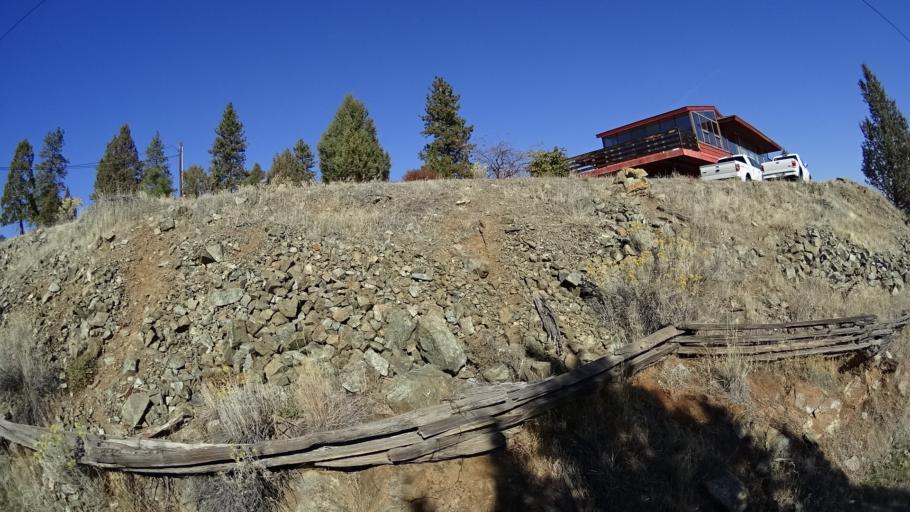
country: US
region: California
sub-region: Siskiyou County
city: Yreka
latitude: 41.7286
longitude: -122.6546
